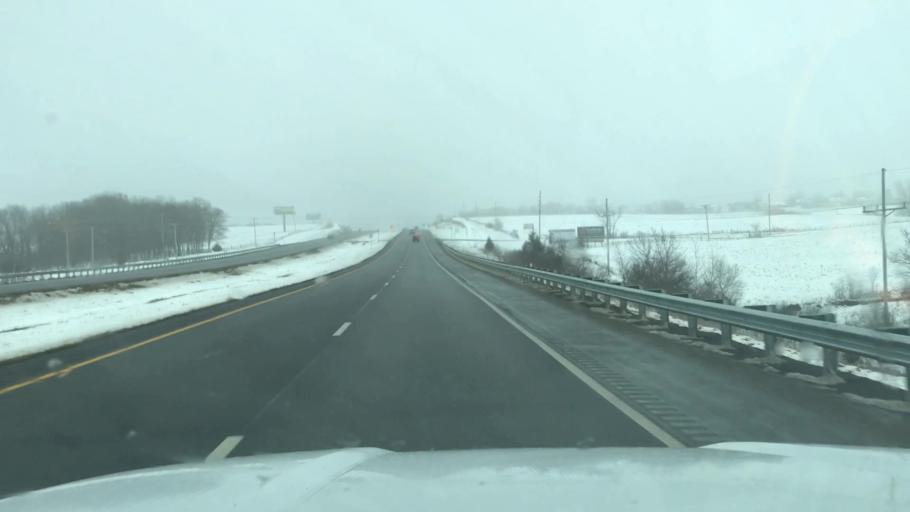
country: US
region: Missouri
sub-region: Clinton County
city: Cameron
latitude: 39.7539
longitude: -94.2653
